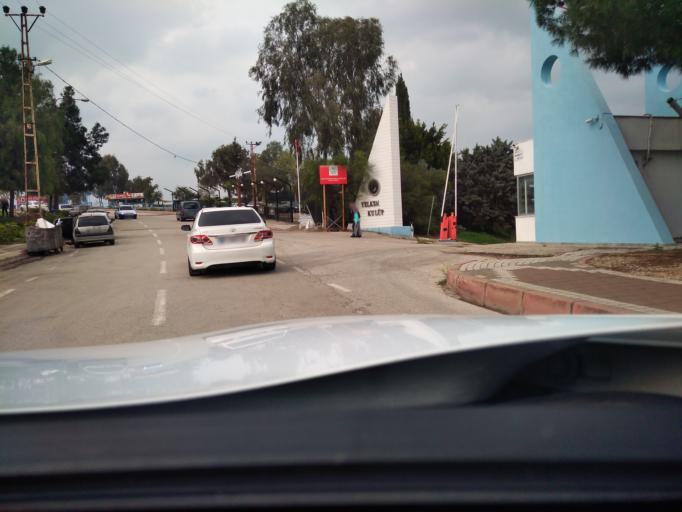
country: TR
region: Adana
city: Adana
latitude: 37.0618
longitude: 35.3021
